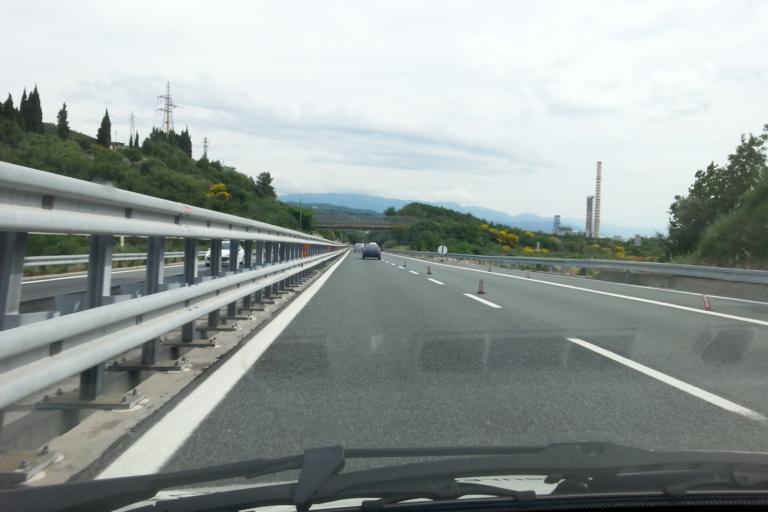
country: IT
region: Liguria
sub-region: Provincia di Savona
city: Valle di Vado
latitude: 44.2672
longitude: 8.4160
